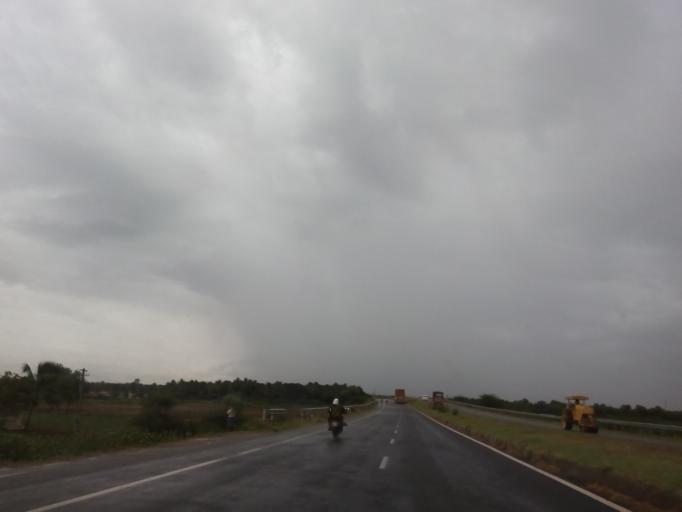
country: IN
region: Karnataka
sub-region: Davanagere
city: Harihar
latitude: 14.4343
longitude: 75.9426
